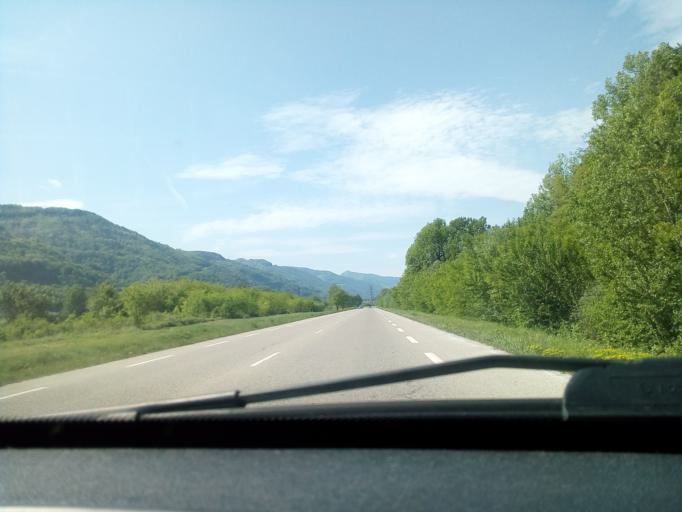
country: FR
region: Rhone-Alpes
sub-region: Departement de l'Isere
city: Froges
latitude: 45.2730
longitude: 5.9153
